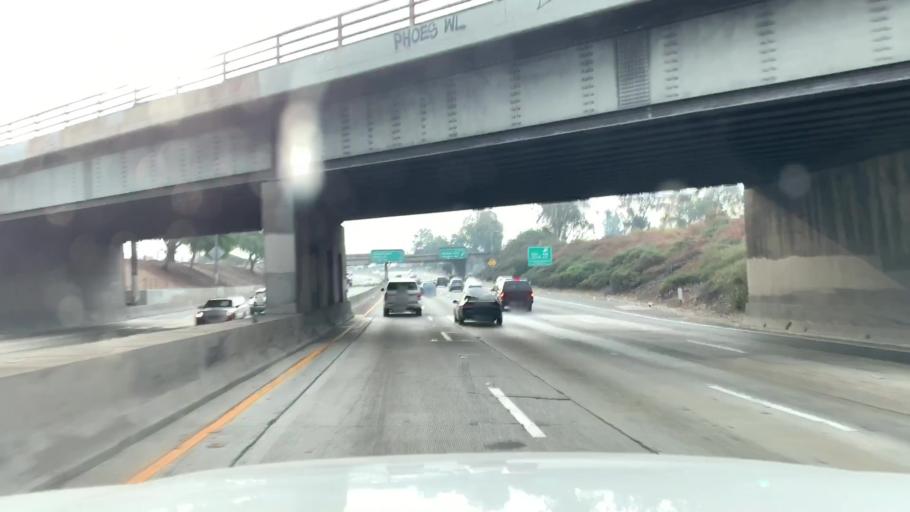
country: US
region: California
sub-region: Los Angeles County
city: Commerce
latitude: 34.0101
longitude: -118.1598
